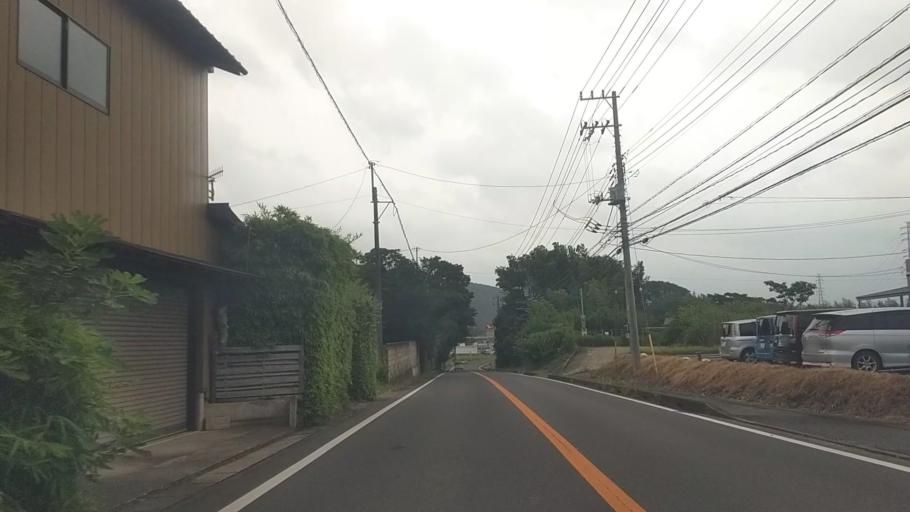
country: JP
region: Chiba
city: Kisarazu
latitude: 35.3115
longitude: 140.0633
